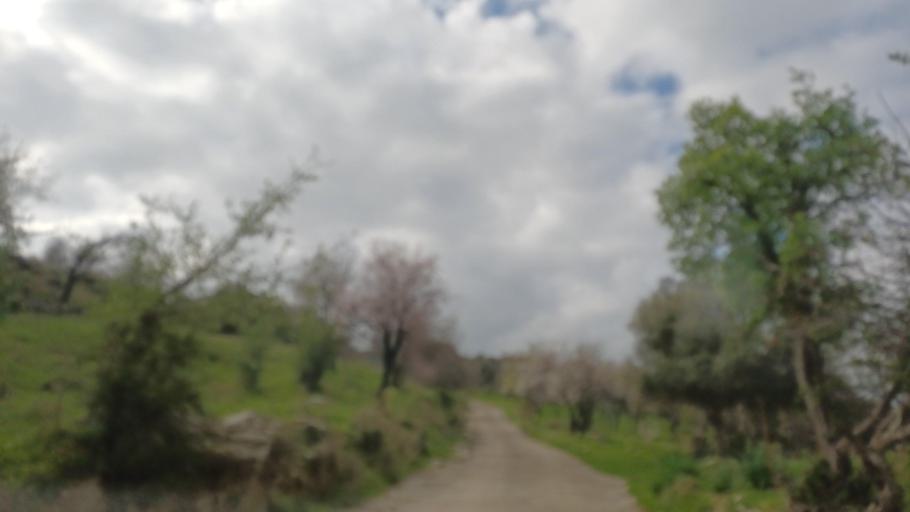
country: CY
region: Limassol
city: Pissouri
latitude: 34.7708
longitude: 32.6655
